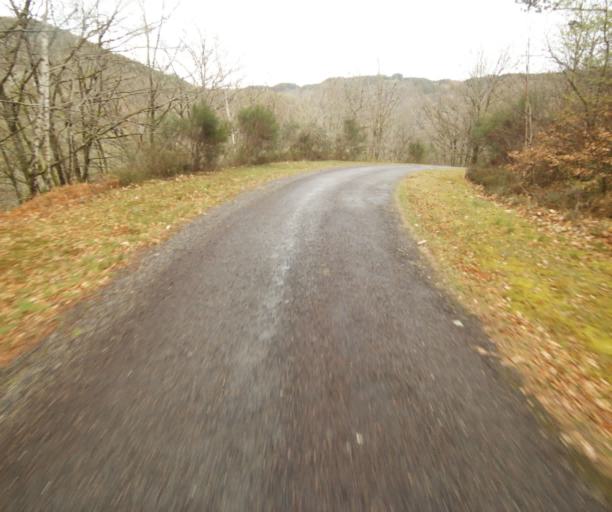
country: FR
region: Limousin
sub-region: Departement de la Correze
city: Saint-Privat
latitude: 45.2139
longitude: 2.0346
